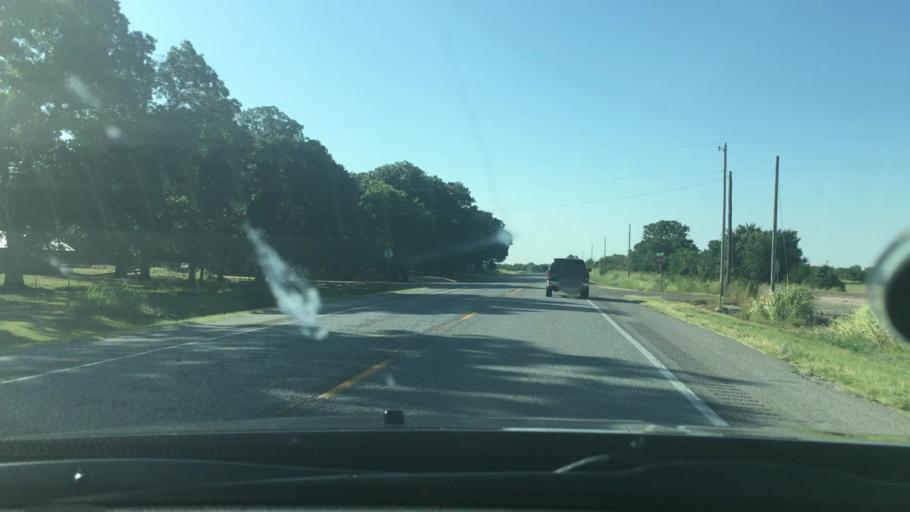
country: US
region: Oklahoma
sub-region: Johnston County
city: Tishomingo
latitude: 34.2602
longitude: -96.7688
